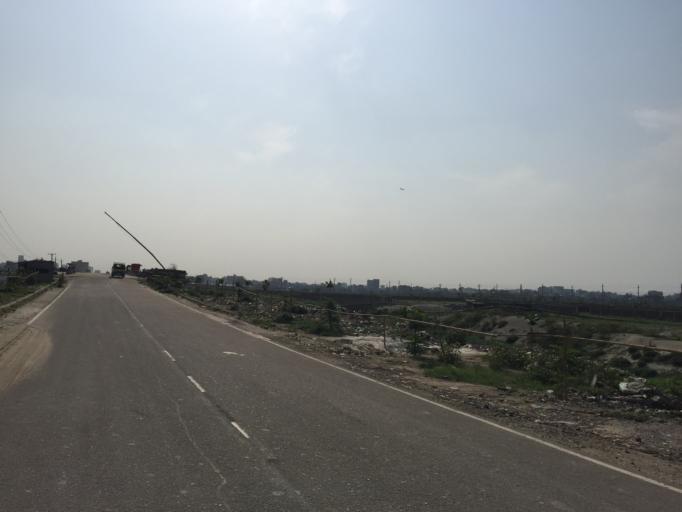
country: BD
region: Dhaka
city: Paltan
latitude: 23.8000
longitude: 90.4467
